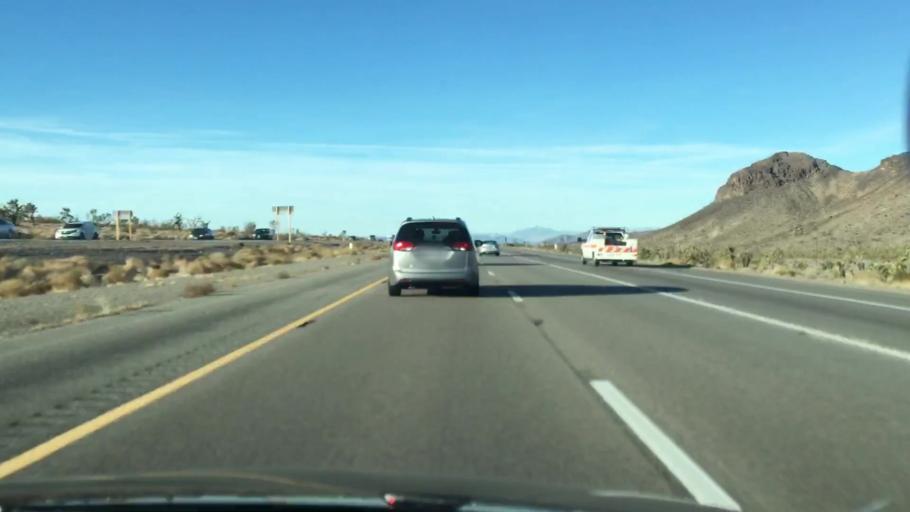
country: US
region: Nevada
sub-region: Clark County
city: Sandy Valley
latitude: 35.3968
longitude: -115.8148
